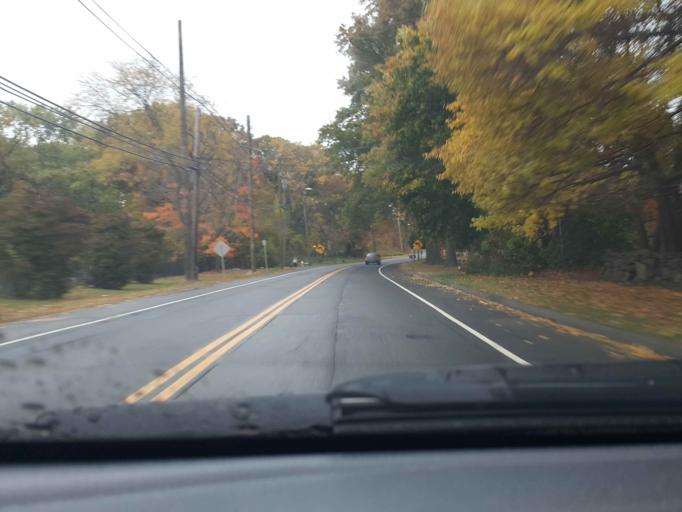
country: US
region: Connecticut
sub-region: New Haven County
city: Madison Center
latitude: 41.2780
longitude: -72.6136
